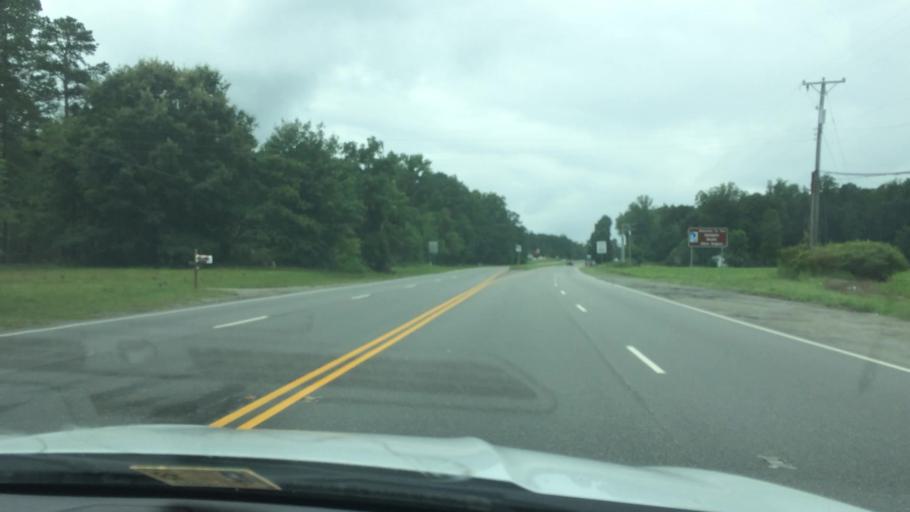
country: US
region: Virginia
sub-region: King William County
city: West Point
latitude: 37.5198
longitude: -76.8315
